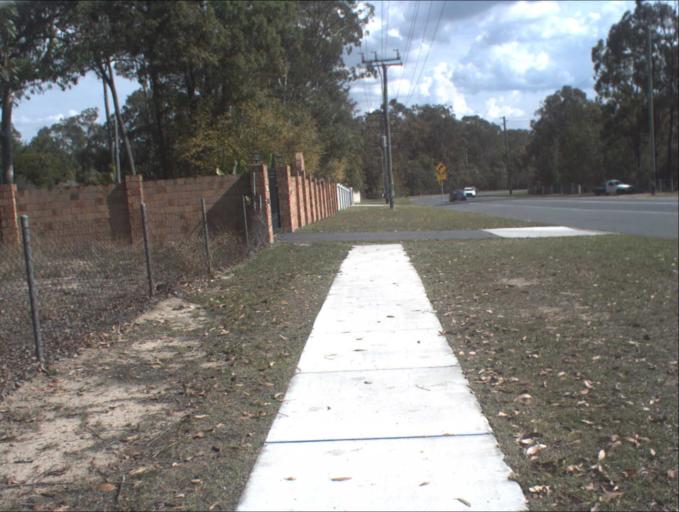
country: AU
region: Queensland
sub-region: Logan
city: Park Ridge South
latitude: -27.7027
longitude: 153.0098
